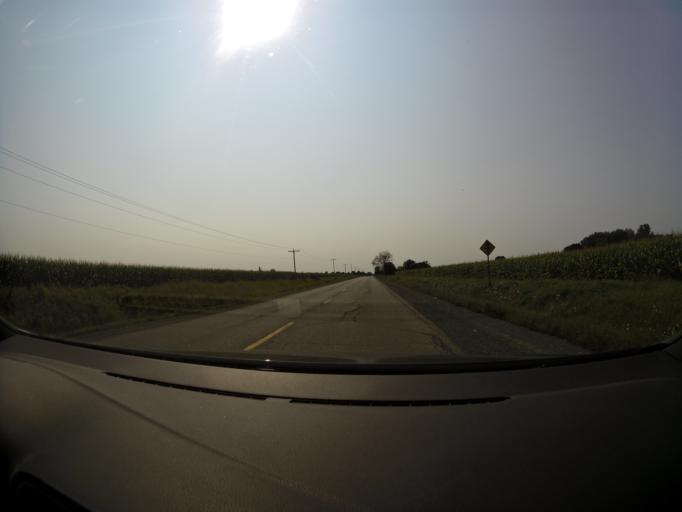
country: CA
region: Ontario
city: Carleton Place
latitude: 45.3410
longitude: -76.0715
